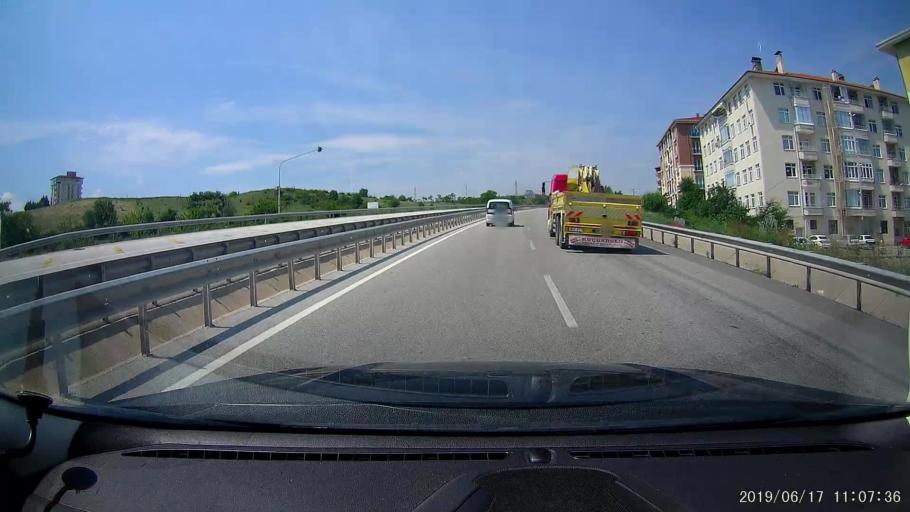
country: TR
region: Kastamonu
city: Tosya
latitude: 41.0002
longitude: 34.0531
